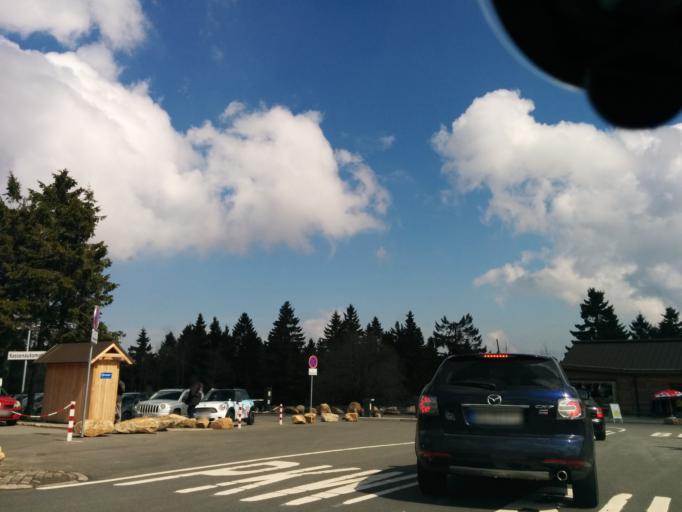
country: DE
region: Lower Saxony
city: Bad Harzburg
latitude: 51.8030
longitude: 10.5364
